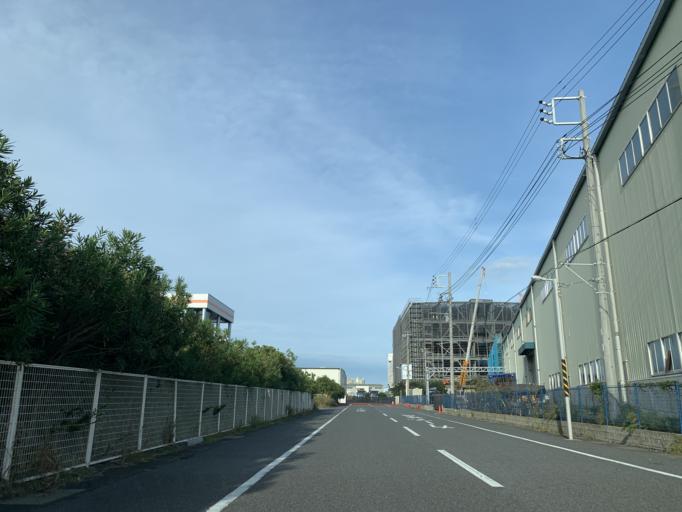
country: JP
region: Tokyo
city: Urayasu
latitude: 35.6257
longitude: 139.9103
